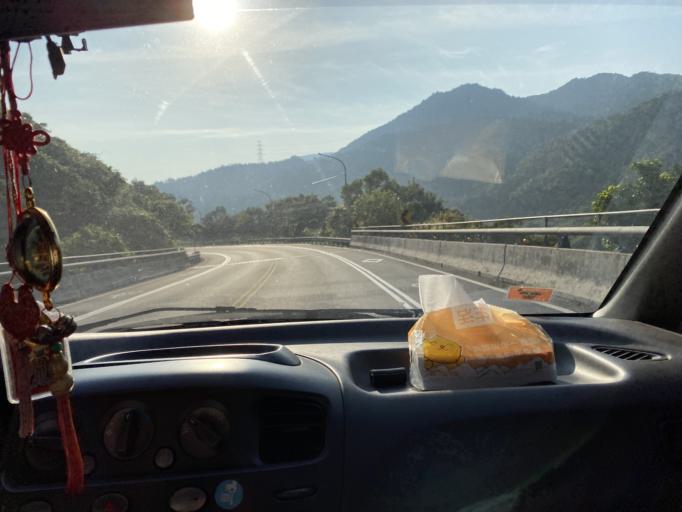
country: TW
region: Taiwan
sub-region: Keelung
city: Keelung
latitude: 25.0188
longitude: 121.8047
